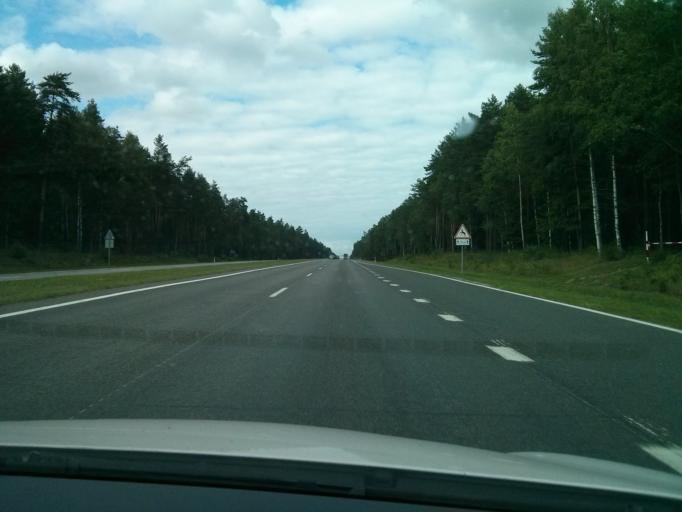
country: BY
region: Minsk
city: Zamostochcha
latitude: 53.8934
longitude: 27.9425
